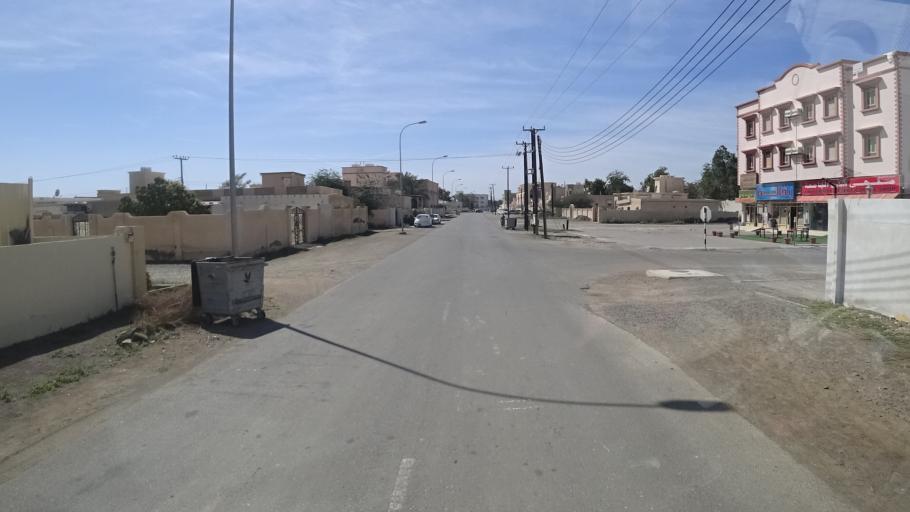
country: OM
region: Al Batinah
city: Al Sohar
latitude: 24.2944
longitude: 56.7861
